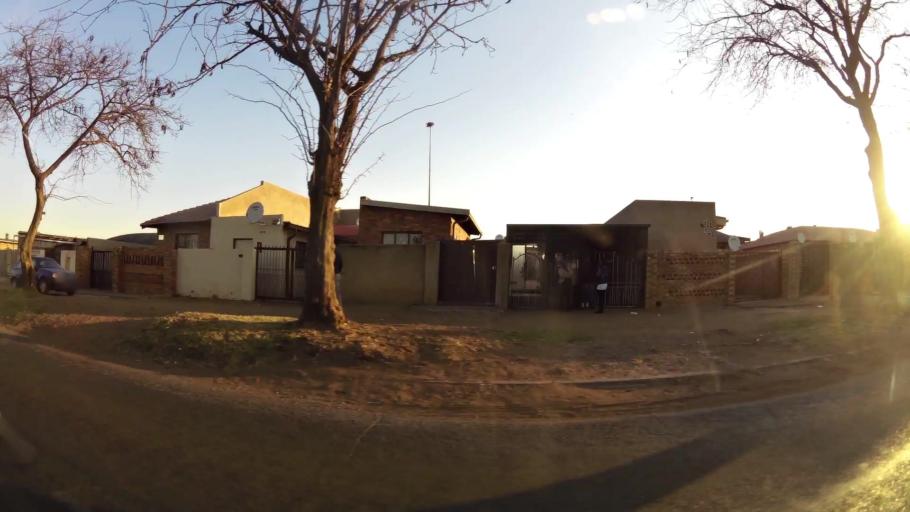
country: ZA
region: Gauteng
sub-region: City of Johannesburg Metropolitan Municipality
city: Soweto
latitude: -26.2429
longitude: 27.8808
